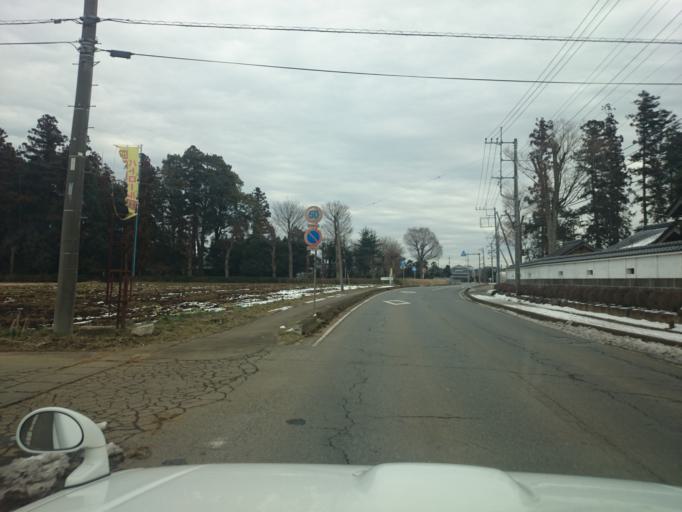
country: JP
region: Ibaraki
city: Tsukuba
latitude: 36.1110
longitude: 140.0651
